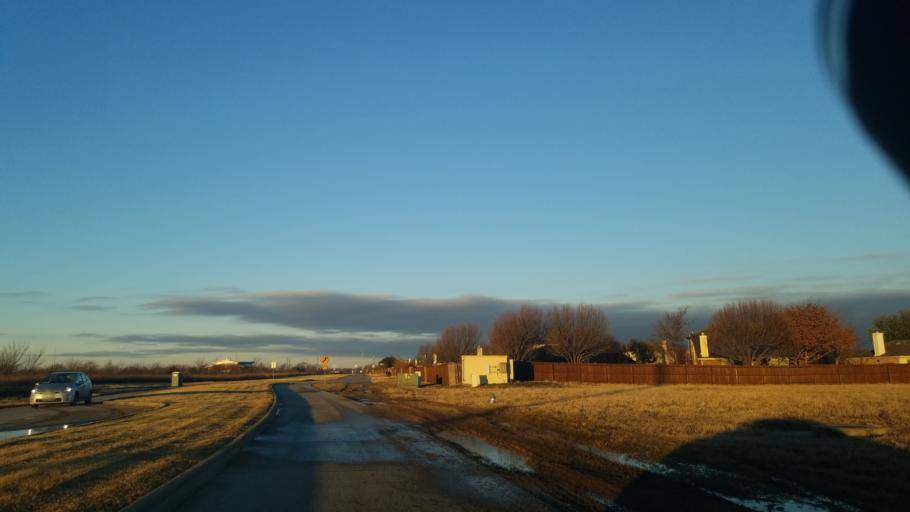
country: US
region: Texas
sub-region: Denton County
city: Argyle
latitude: 33.1703
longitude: -97.1683
